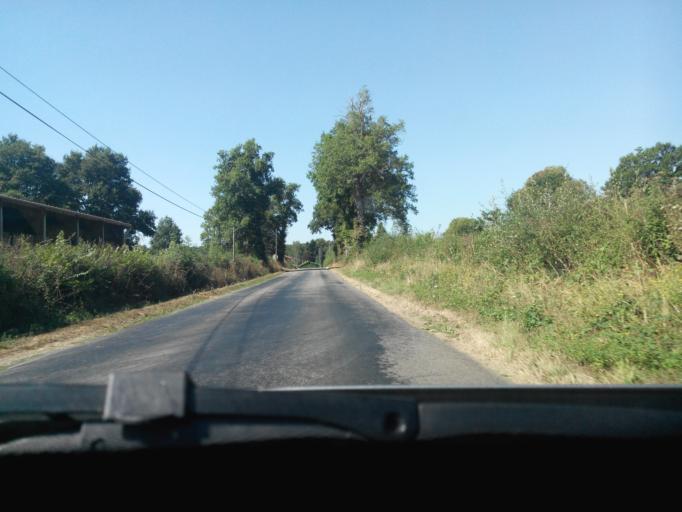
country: FR
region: Poitou-Charentes
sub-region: Departement de la Charente
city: Etagnac
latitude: 45.9452
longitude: 0.7802
